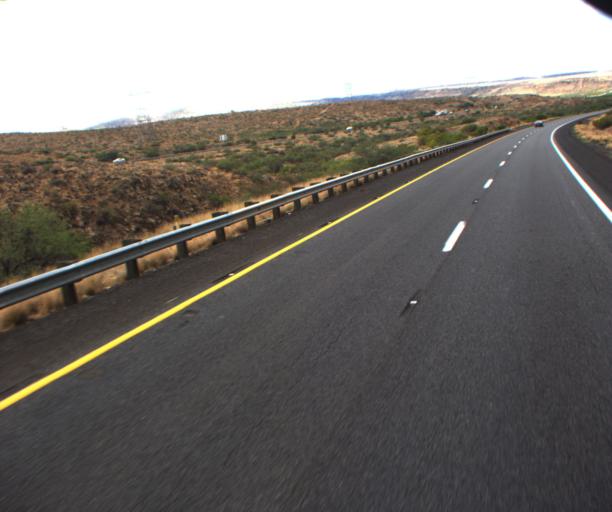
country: US
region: Arizona
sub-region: Yavapai County
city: Cordes Lakes
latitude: 34.2542
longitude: -112.1144
